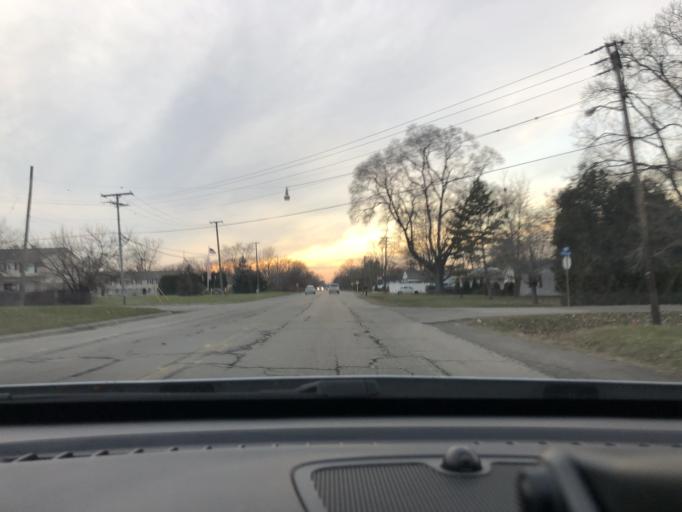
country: US
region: Michigan
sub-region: Wayne County
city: Allen Park
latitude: 42.2421
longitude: -83.2322
